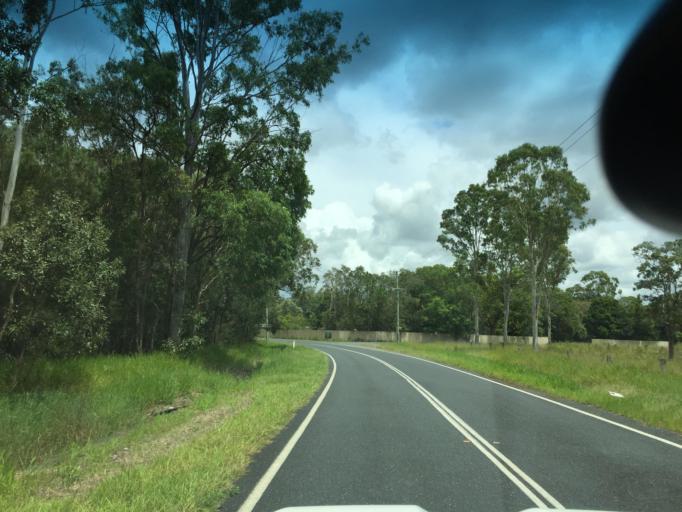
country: AU
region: Queensland
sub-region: Moreton Bay
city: Caboolture
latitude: -27.0463
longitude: 152.9130
